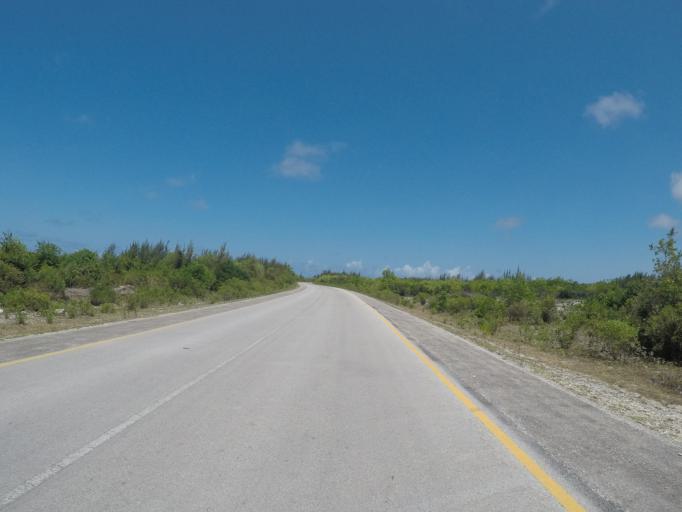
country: TZ
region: Zanzibar Central/South
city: Nganane
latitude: -6.3943
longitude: 39.5590
